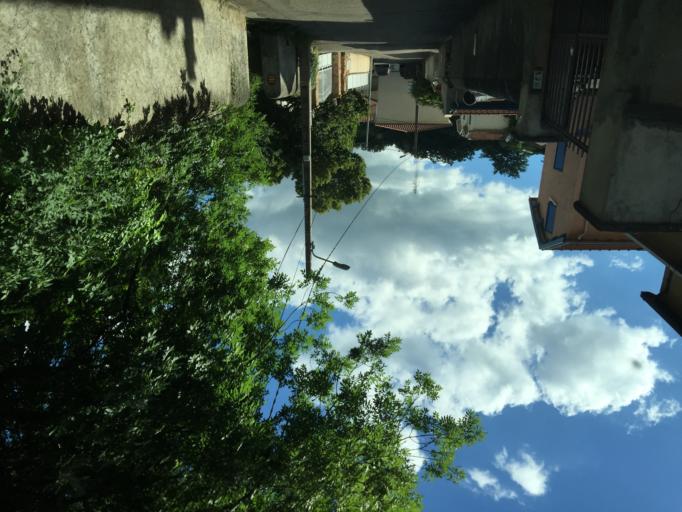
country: FR
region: Rhone-Alpes
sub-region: Departement de la Loire
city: Saint-Chamond
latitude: 45.4747
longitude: 4.4990
